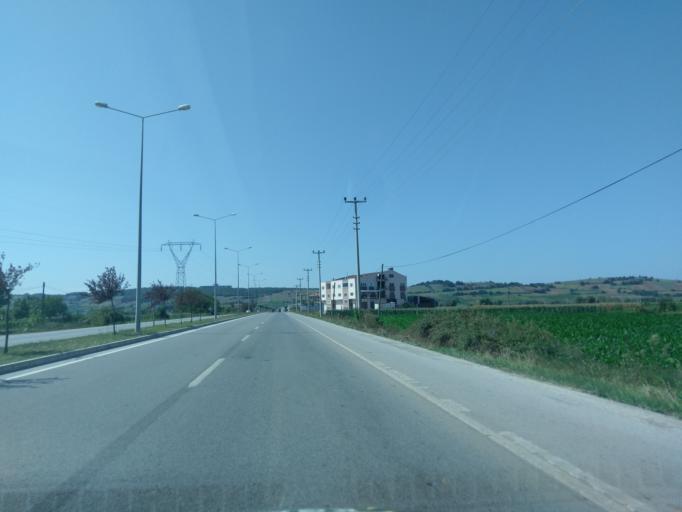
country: TR
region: Samsun
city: Bafra
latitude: 41.5754
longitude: 35.8605
